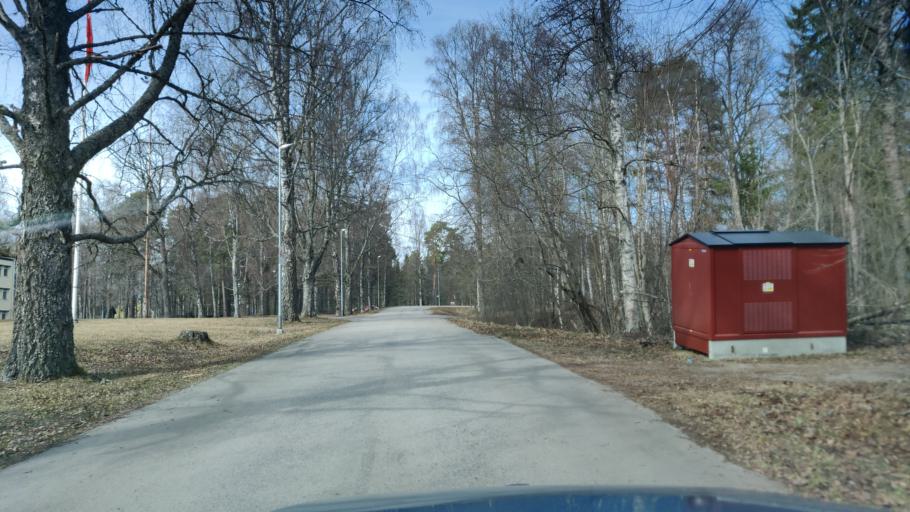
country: SE
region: Vaermland
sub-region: Hagfors Kommun
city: Hagfors
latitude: 60.0191
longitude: 13.6196
